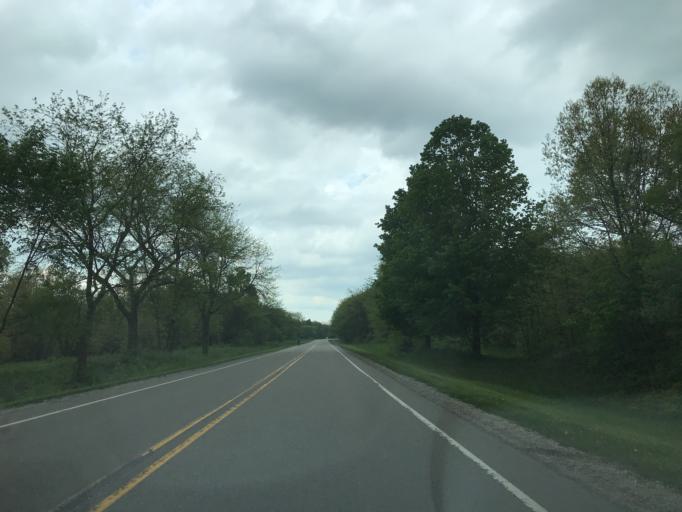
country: US
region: Michigan
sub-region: Oakland County
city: South Lyon
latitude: 42.5298
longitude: -83.6338
